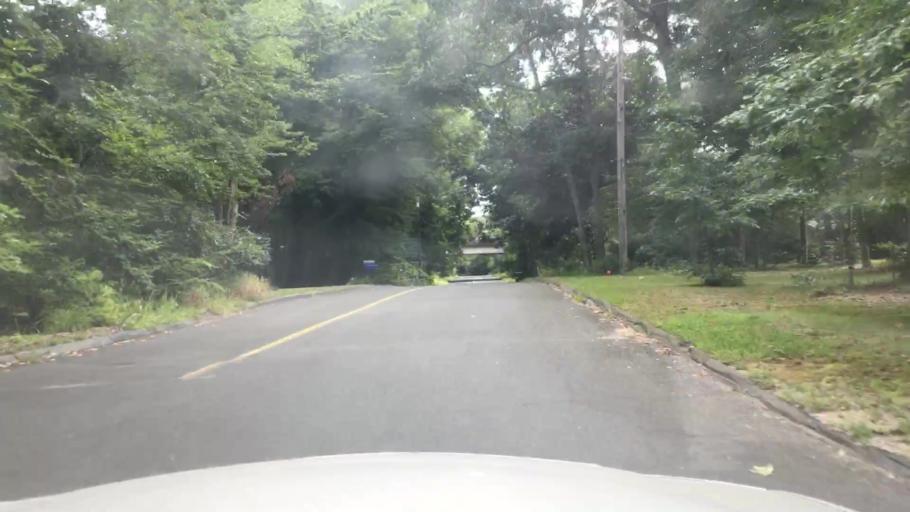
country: US
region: Connecticut
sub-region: Middlesex County
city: Essex Village
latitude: 41.3375
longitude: -72.3978
